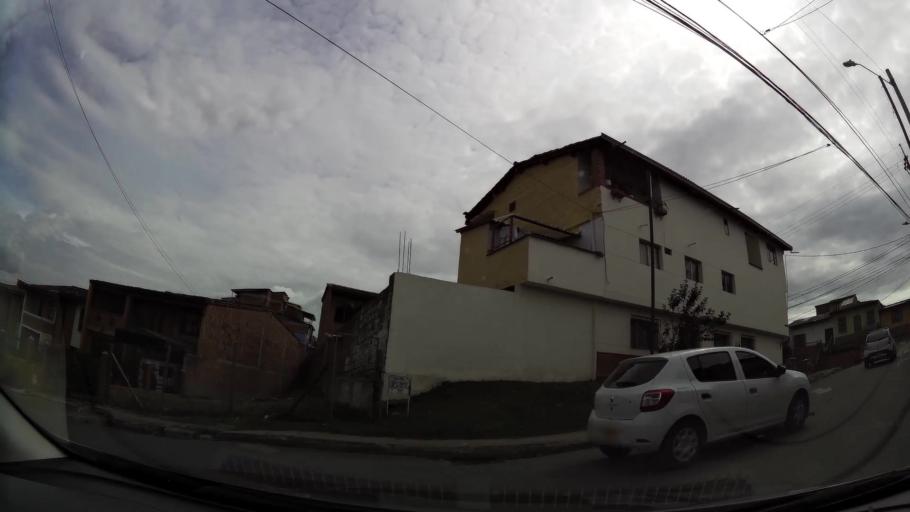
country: CO
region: Antioquia
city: Rionegro
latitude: 6.1591
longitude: -75.3736
